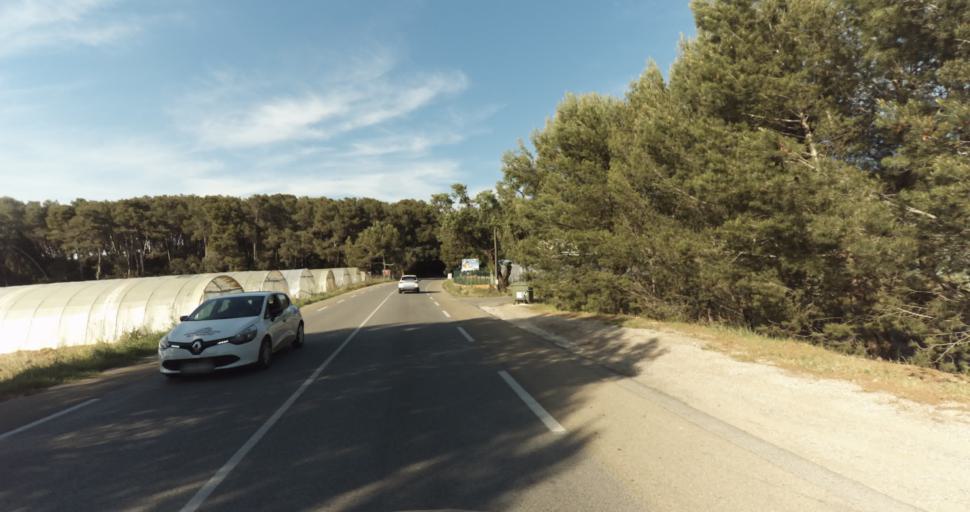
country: FR
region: Provence-Alpes-Cote d'Azur
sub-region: Departement du Var
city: Carqueiranne
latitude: 43.1128
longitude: 6.0538
